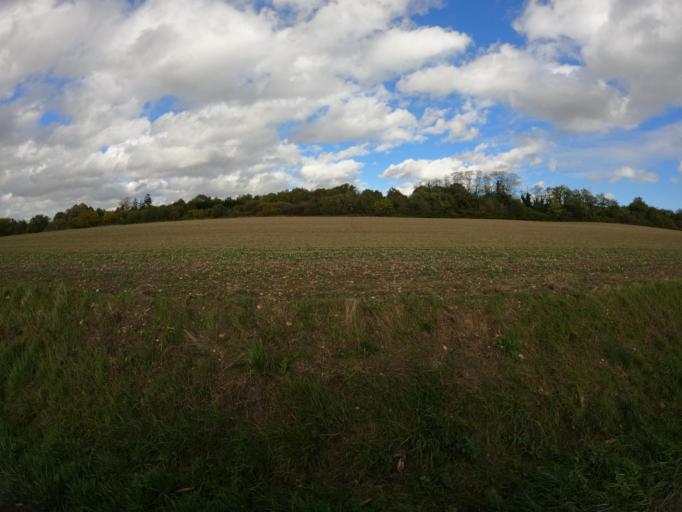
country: FR
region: Ile-de-France
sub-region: Departement de Seine-et-Marne
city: Coupvray
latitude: 48.8997
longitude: 2.7845
